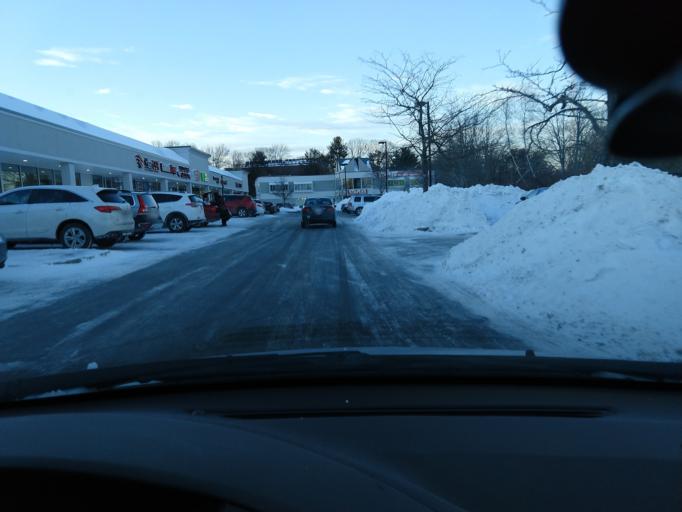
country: US
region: Massachusetts
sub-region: Middlesex County
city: Burlington
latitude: 42.4855
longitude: -71.2196
